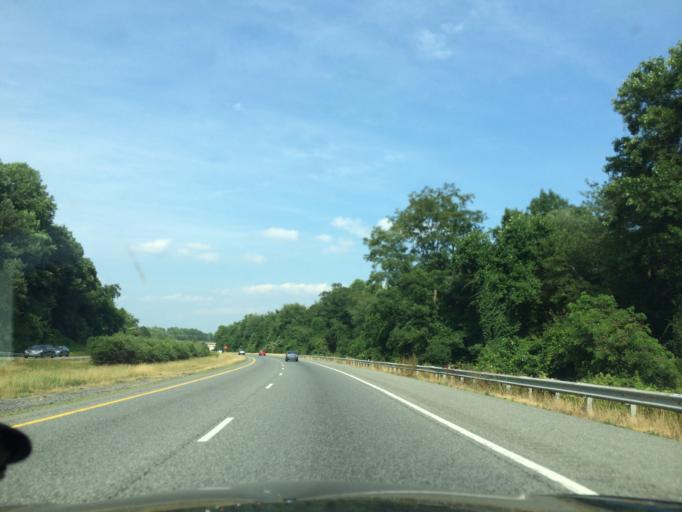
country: US
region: Maryland
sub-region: Howard County
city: Columbia
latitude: 39.3021
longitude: -76.9057
